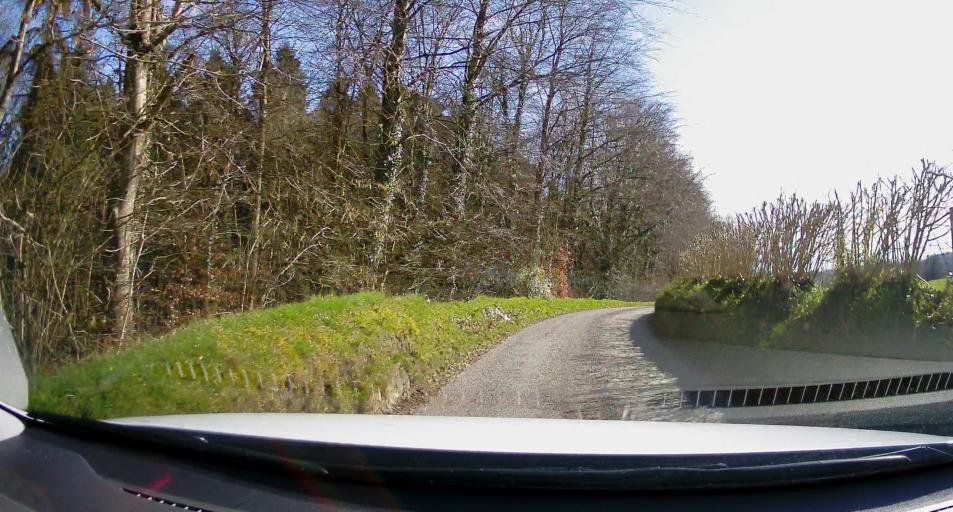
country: GB
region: Wales
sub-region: County of Ceredigion
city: Lledrod
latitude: 52.3377
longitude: -3.9576
